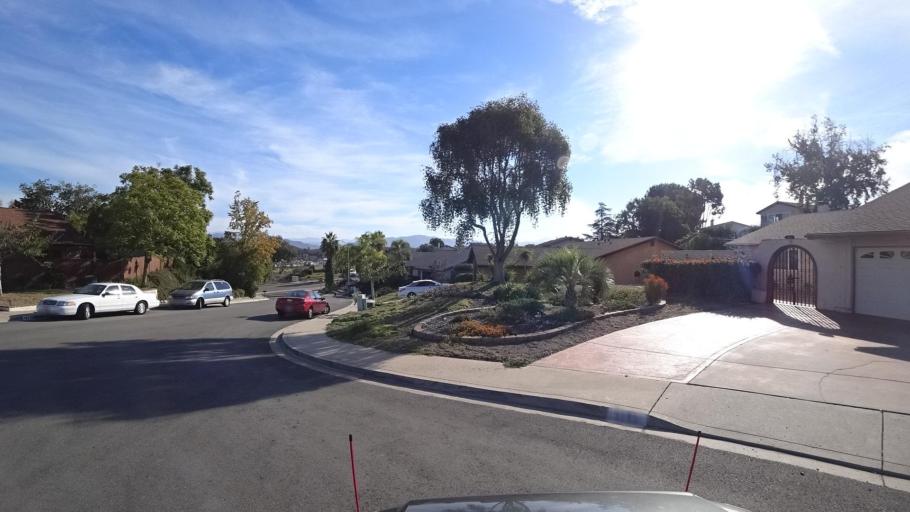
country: US
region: California
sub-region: San Diego County
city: Casa de Oro-Mount Helix
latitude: 32.7436
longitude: -116.9616
